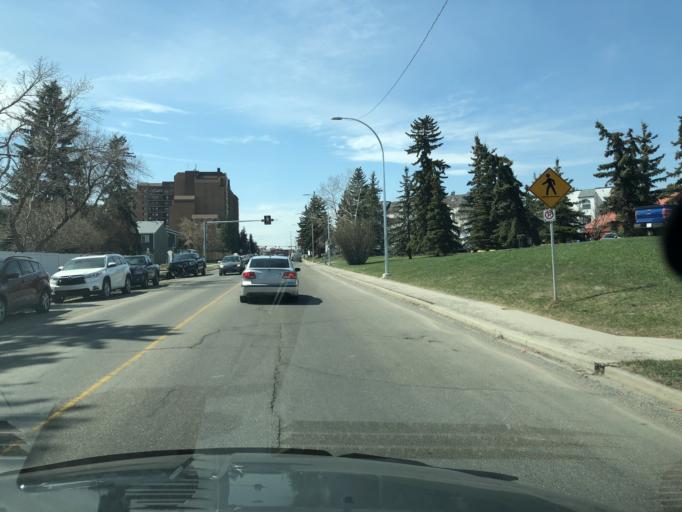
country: CA
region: Alberta
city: Calgary
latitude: 50.9723
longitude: -114.0644
